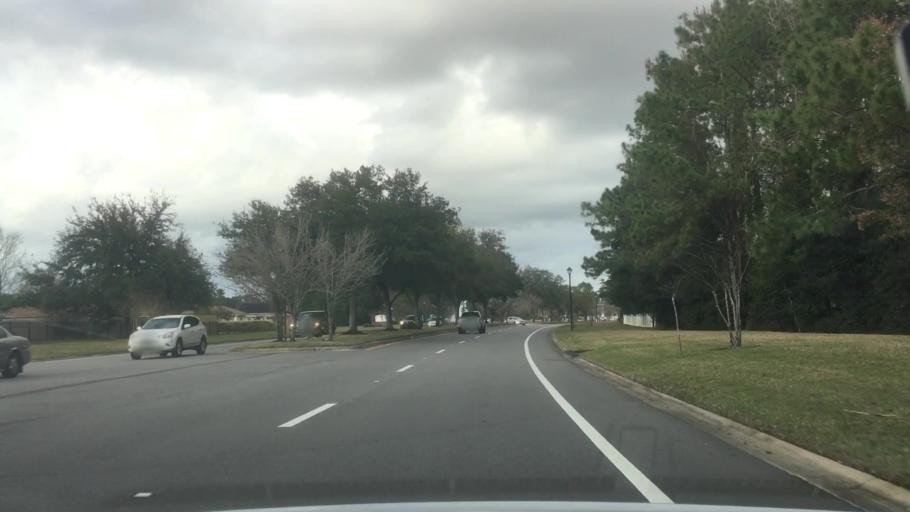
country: US
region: Florida
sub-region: Duval County
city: Atlantic Beach
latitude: 30.3205
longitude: -81.5083
